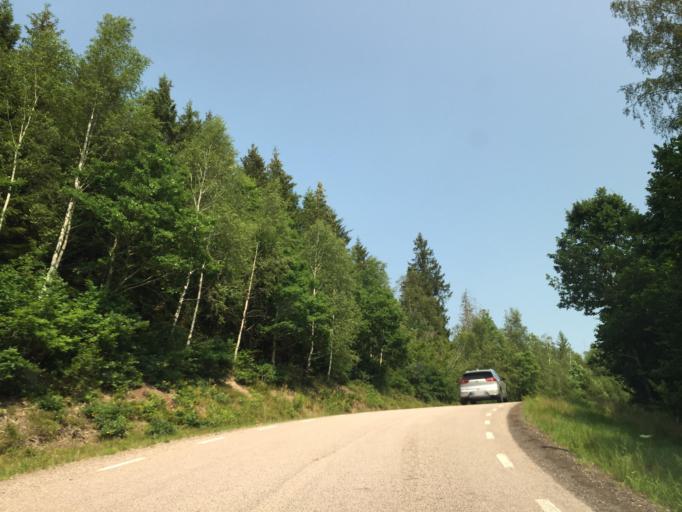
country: SE
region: Vaestra Goetaland
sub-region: Lilla Edets Kommun
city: Lilla Edet
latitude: 58.1553
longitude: 12.0611
